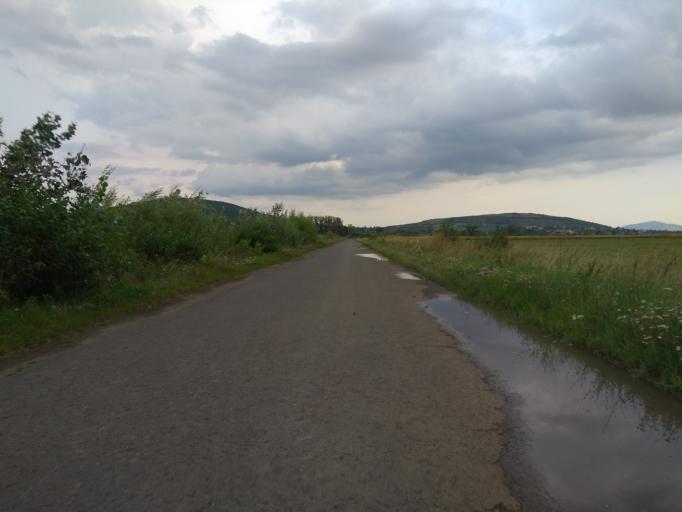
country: HU
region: Borsod-Abauj-Zemplen
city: Bekecs
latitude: 48.1573
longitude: 21.1303
